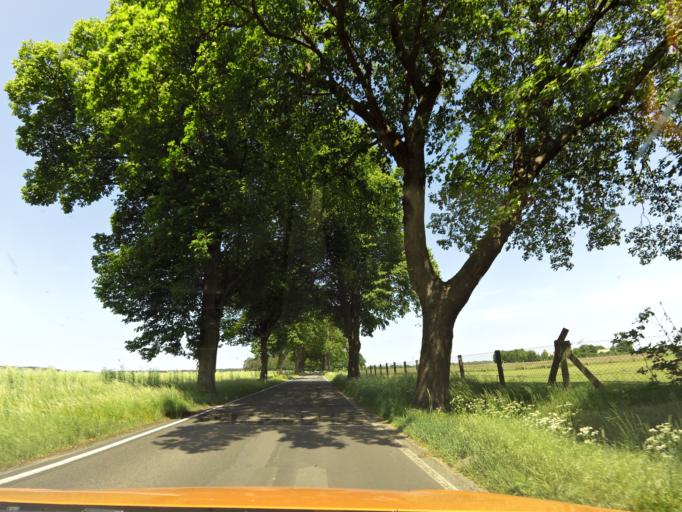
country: DE
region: Mecklenburg-Vorpommern
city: Siggelkow
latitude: 53.3895
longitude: 11.9346
